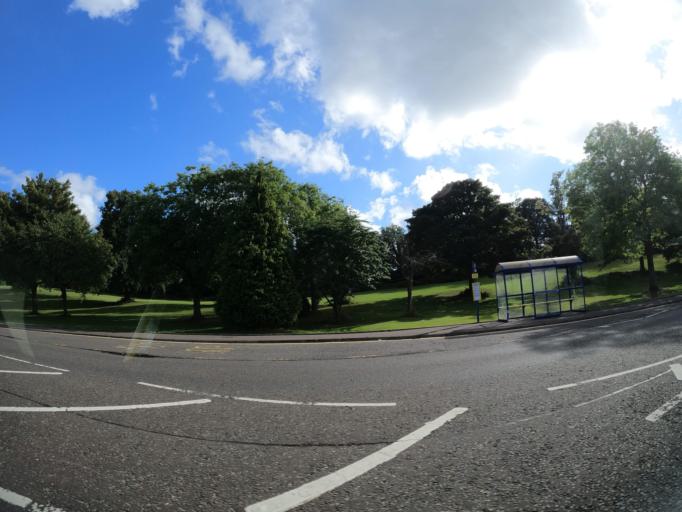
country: GB
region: Scotland
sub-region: Falkirk
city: Falkirk
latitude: 55.9968
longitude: -3.7599
